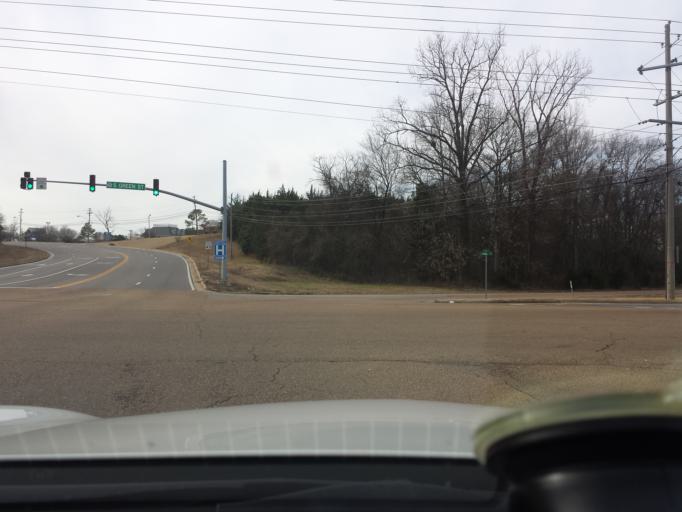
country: US
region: Mississippi
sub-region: Lee County
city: Tupelo
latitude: 34.2362
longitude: -88.7108
